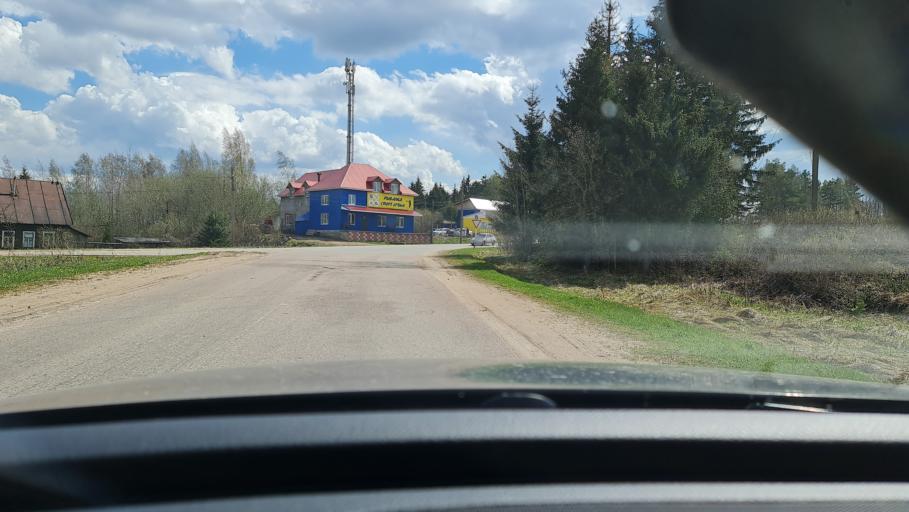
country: RU
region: Tverskaya
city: Toropets
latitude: 56.4734
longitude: 31.6382
